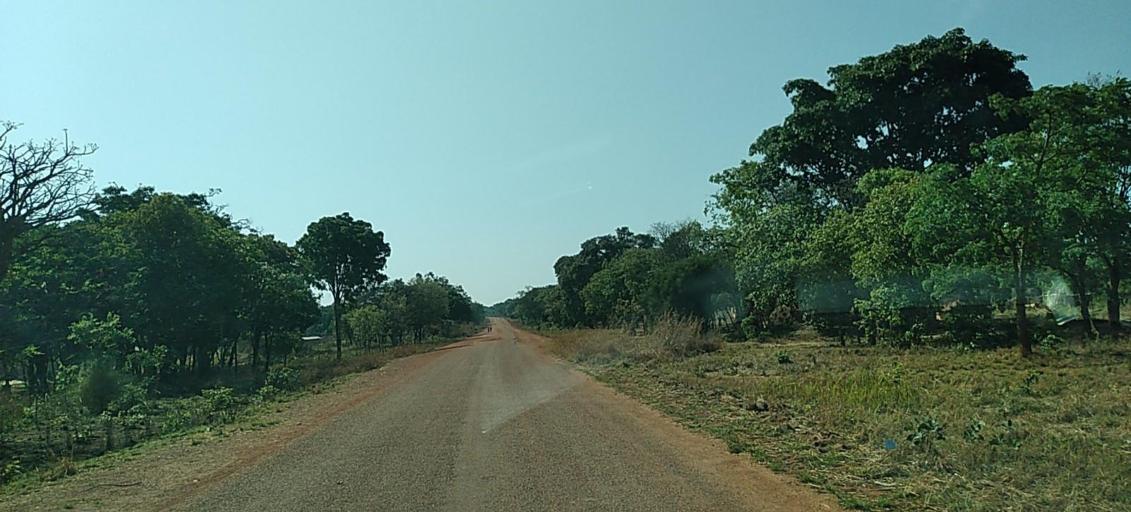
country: ZM
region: North-Western
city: Mwinilunga
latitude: -11.8940
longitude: 25.2702
